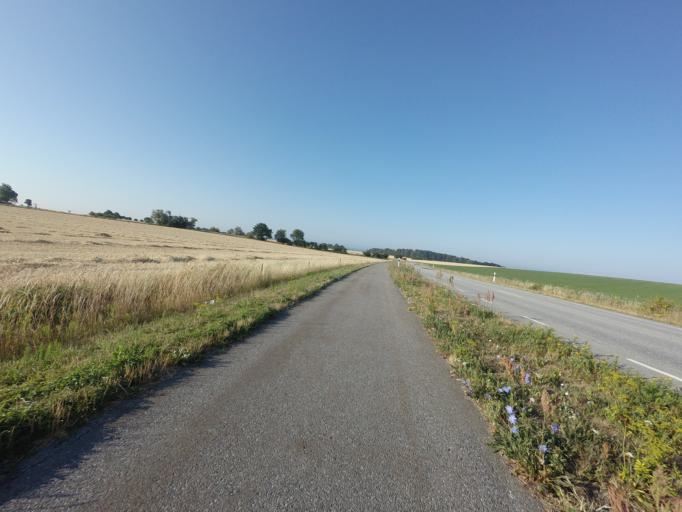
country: SE
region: Skane
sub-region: Helsingborg
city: Glumslov
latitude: 55.9255
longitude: 12.8179
